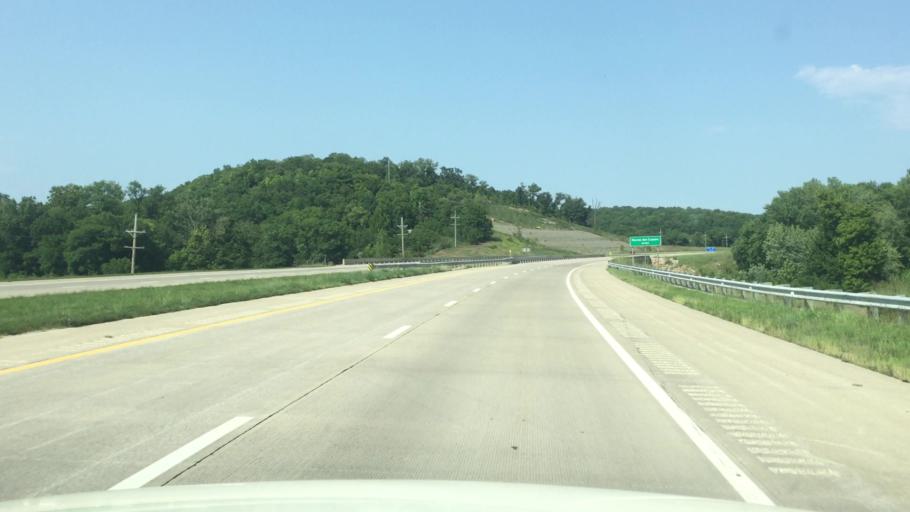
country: US
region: Kansas
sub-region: Linn County
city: Pleasanton
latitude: 38.2475
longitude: -94.6872
